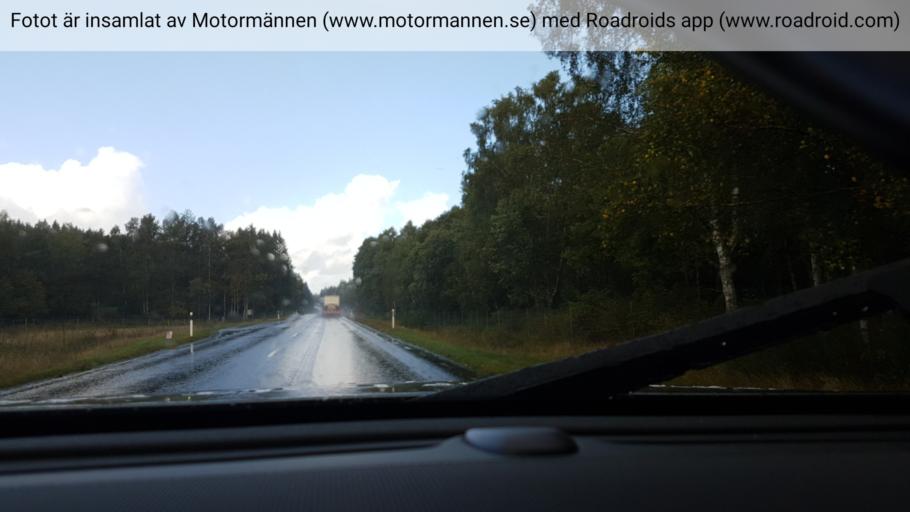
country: SE
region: Vaestra Goetaland
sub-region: Alingsas Kommun
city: Alingsas
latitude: 57.9923
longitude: 12.4418
